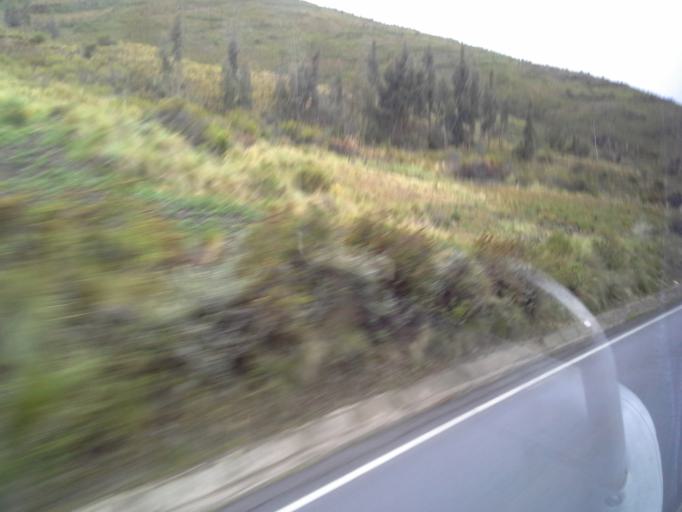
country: BO
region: Cochabamba
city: Colomi
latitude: -17.3936
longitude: -65.8540
